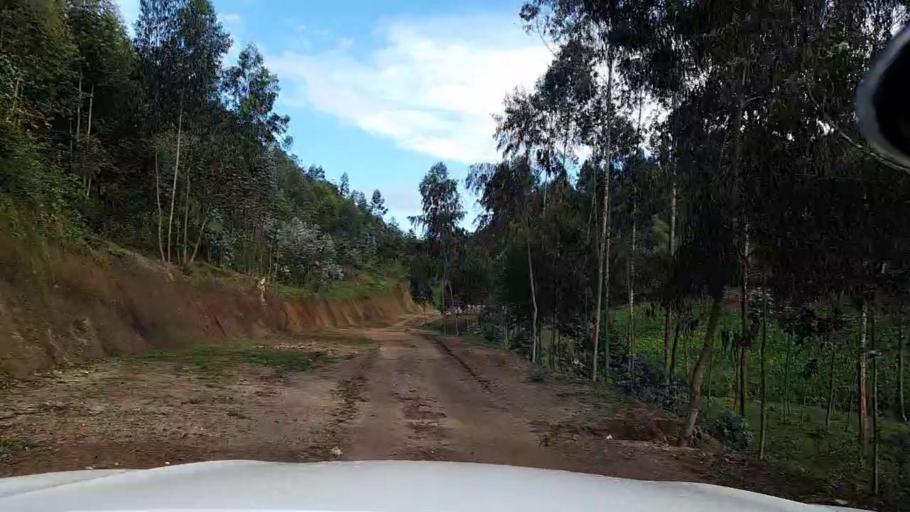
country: BI
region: Kayanza
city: Kayanza
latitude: -2.7806
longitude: 29.4513
